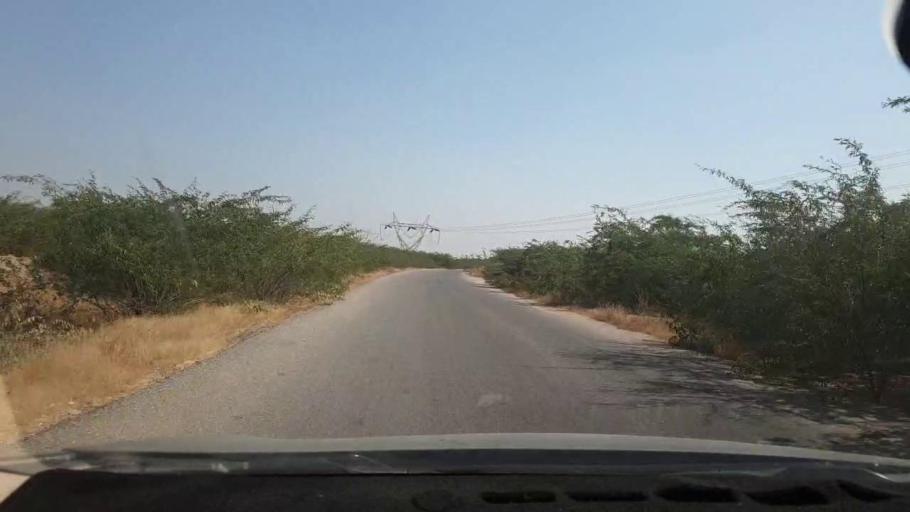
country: PK
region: Sindh
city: Malir Cantonment
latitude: 25.1439
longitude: 67.1912
